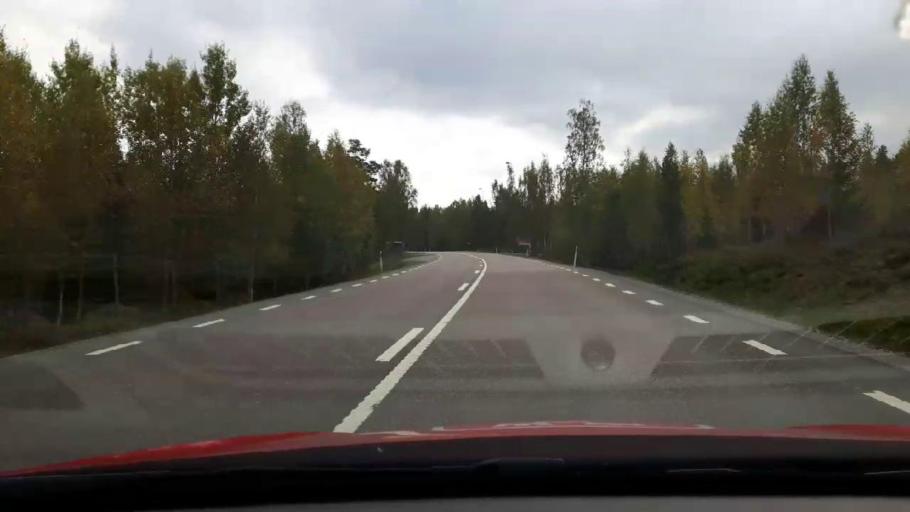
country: SE
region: Gaevleborg
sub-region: Bollnas Kommun
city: Kilafors
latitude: 61.2764
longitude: 16.5248
